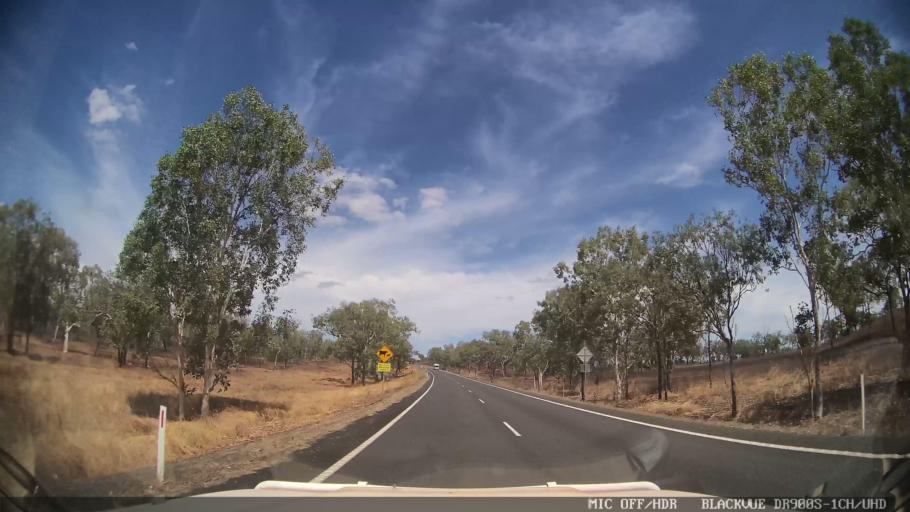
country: AU
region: Queensland
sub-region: Cook
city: Cooktown
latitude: -15.8010
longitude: 144.9229
